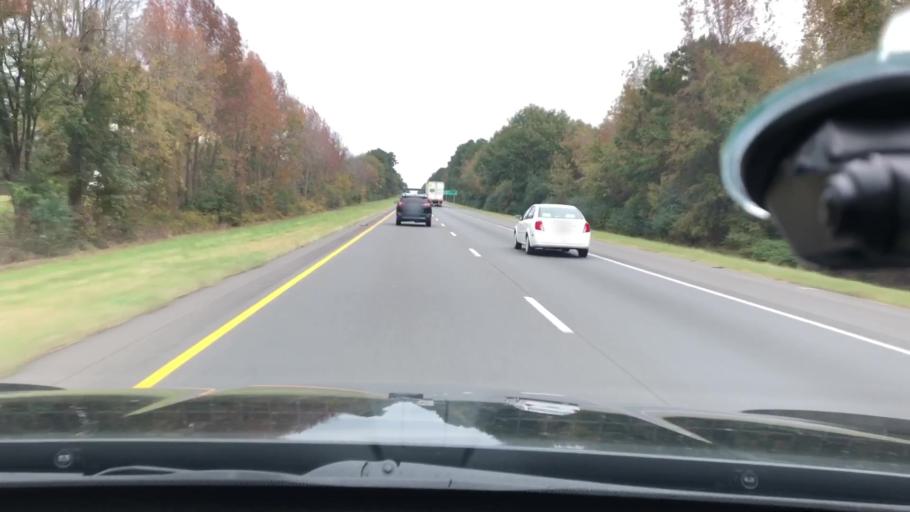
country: US
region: Arkansas
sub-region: Hempstead County
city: Hope
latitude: 33.6981
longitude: -93.5882
